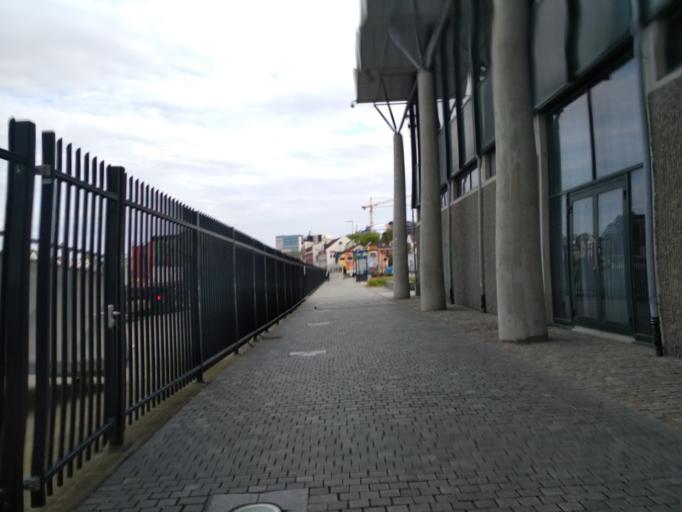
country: NO
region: Rogaland
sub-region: Stavanger
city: Stavanger
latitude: 58.9745
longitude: 5.7253
